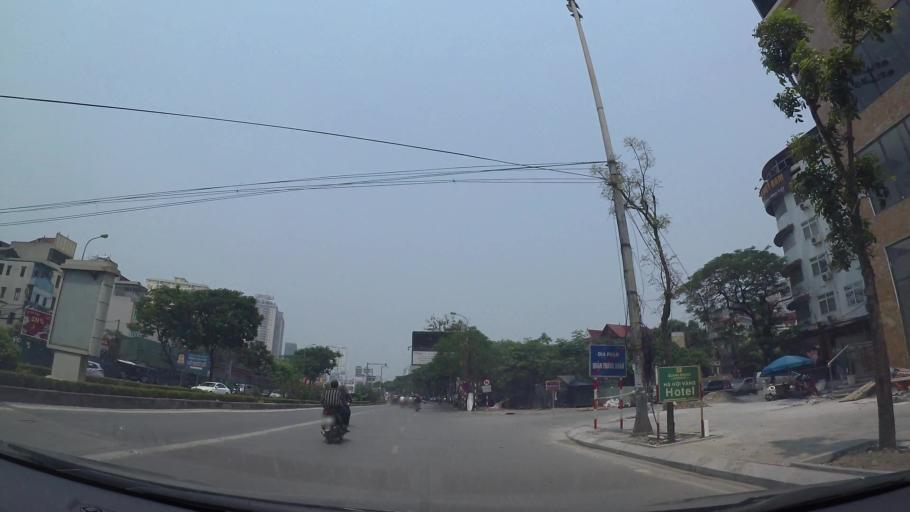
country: VN
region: Ha Noi
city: Thanh Xuan
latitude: 21.0078
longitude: 105.8086
